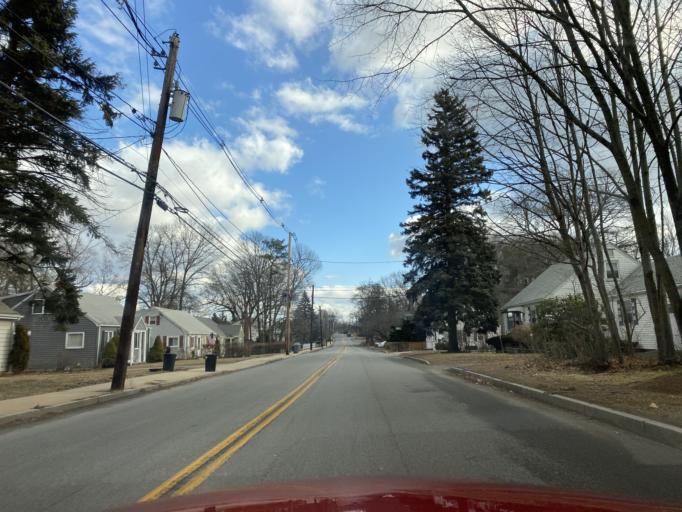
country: US
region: Massachusetts
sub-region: Middlesex County
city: Woburn
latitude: 42.4810
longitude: -71.1328
